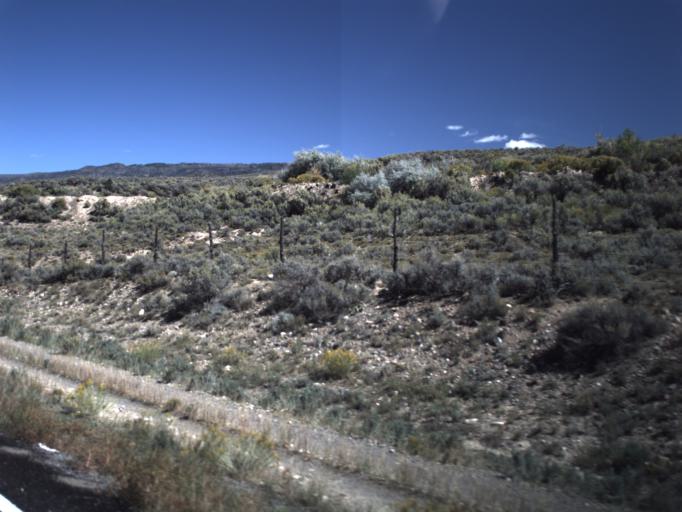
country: US
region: Utah
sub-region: Piute County
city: Junction
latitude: 38.1325
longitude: -111.9991
